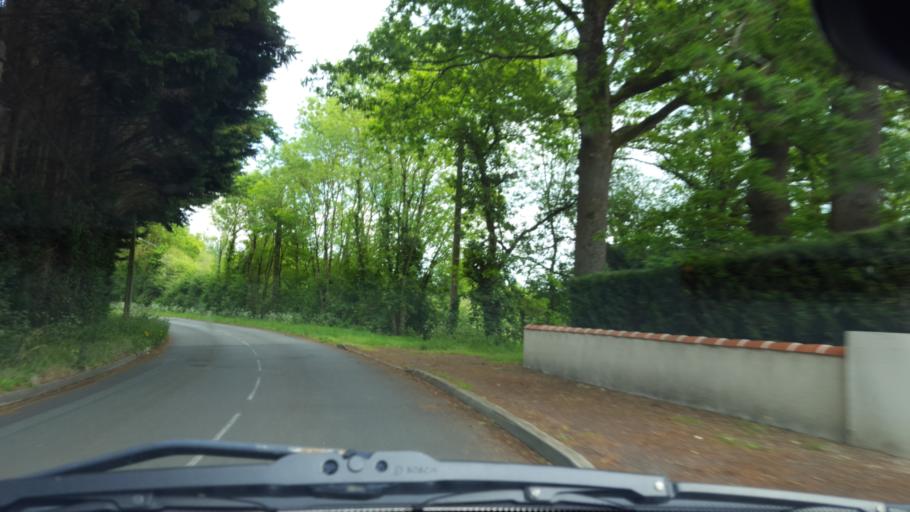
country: FR
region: Pays de la Loire
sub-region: Departement de la Loire-Atlantique
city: Saint-Philbert-de-Grand-Lieu
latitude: 47.0356
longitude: -1.6311
